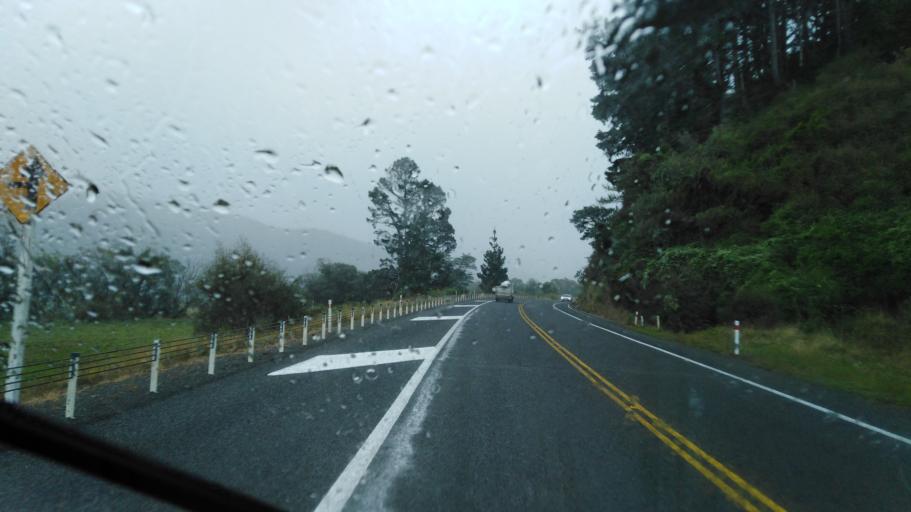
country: NZ
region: Marlborough
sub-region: Marlborough District
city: Picton
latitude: -41.3749
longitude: 173.9469
